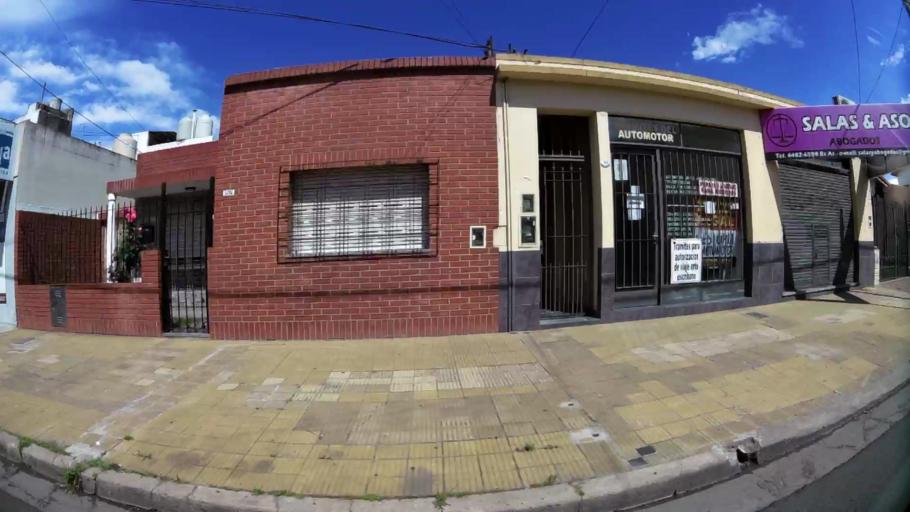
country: AR
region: Buenos Aires
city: San Justo
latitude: -34.6752
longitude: -58.5675
